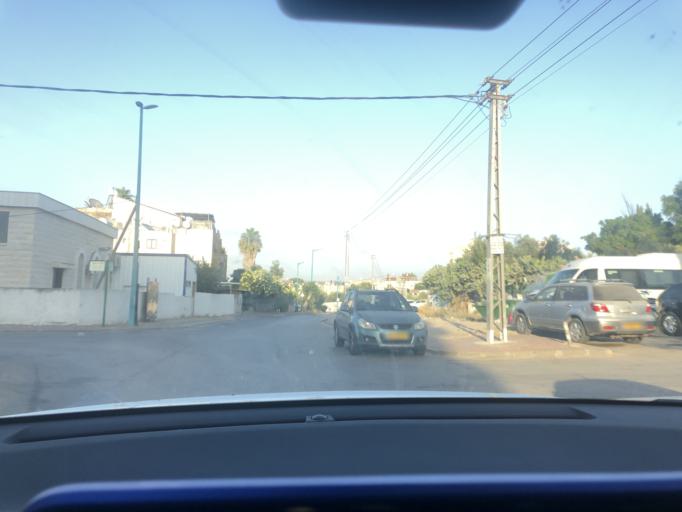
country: IL
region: Central District
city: Lod
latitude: 31.9536
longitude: 34.9025
